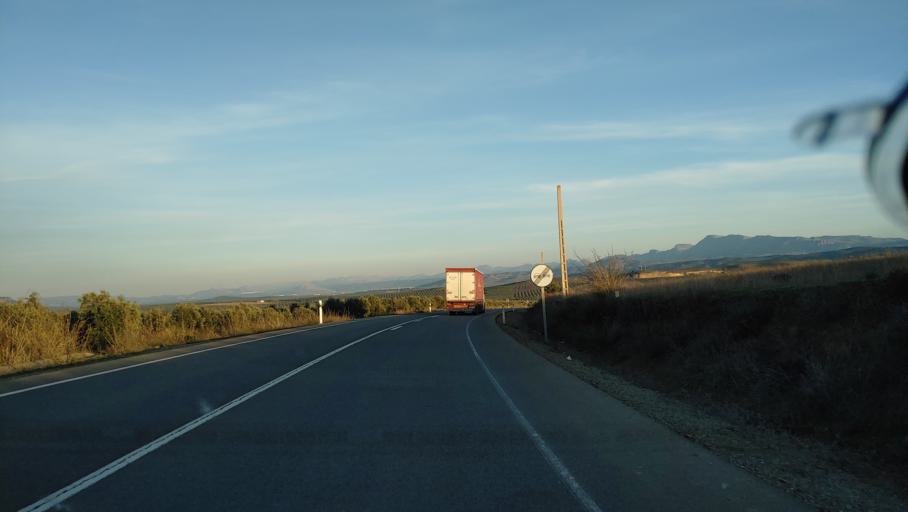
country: ES
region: Andalusia
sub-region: Provincia de Malaga
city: Campillos
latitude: 37.0534
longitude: -4.7809
